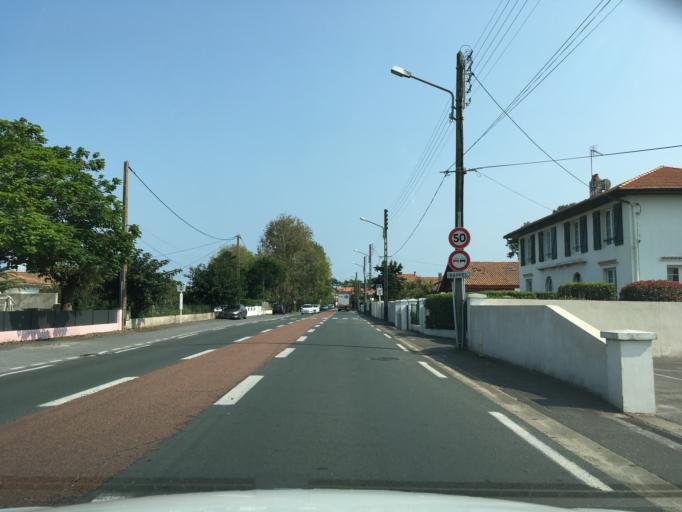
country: FR
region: Aquitaine
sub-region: Departement des Pyrenees-Atlantiques
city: Boucau
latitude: 43.5261
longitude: -1.5114
